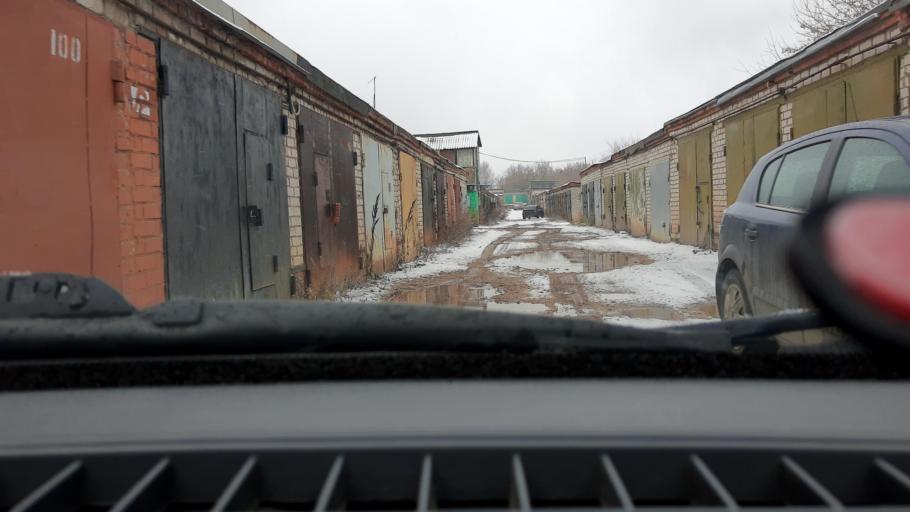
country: RU
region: Bashkortostan
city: Ufa
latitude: 54.8026
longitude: 56.0400
